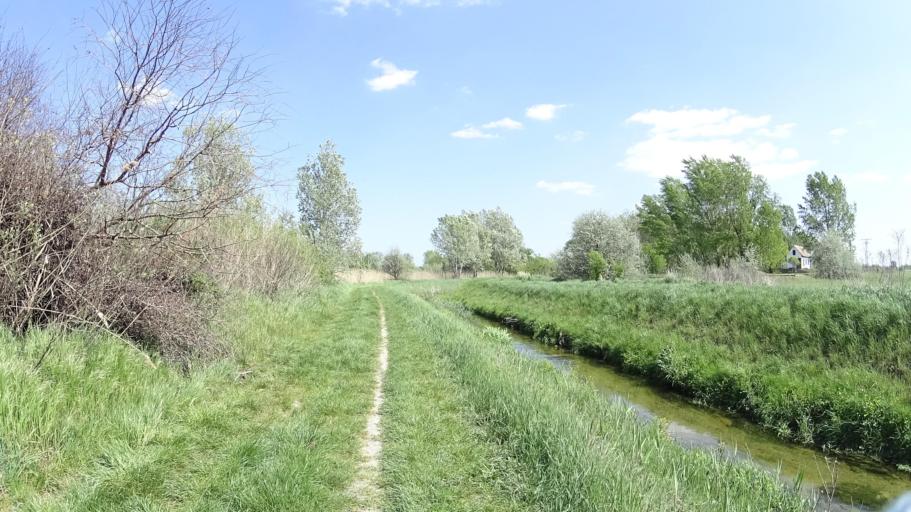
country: HU
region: Pest
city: Vecses
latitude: 47.3976
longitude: 19.2849
